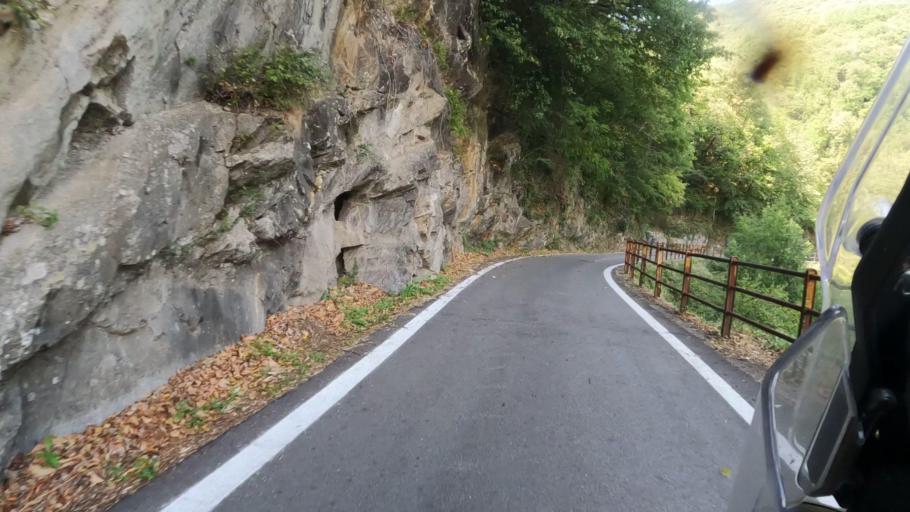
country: IT
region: Lombardy
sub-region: Provincia di Varese
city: Agra
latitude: 46.0557
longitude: 8.7667
